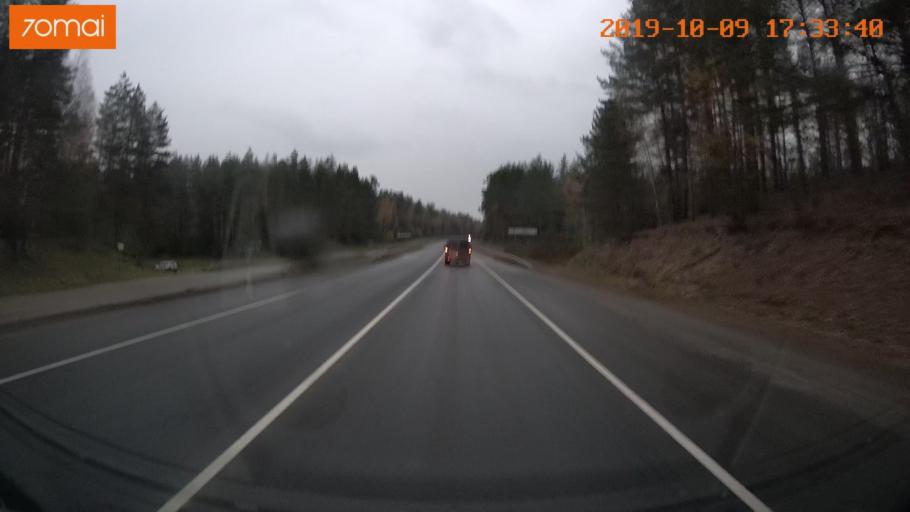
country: RU
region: Ivanovo
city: Bogorodskoye
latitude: 57.1151
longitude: 41.0183
